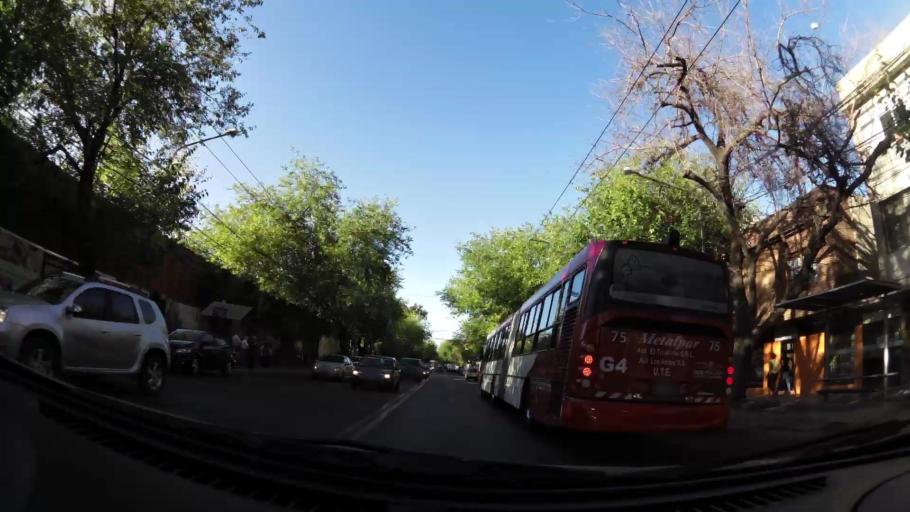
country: AR
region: Mendoza
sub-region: Departamento de Godoy Cruz
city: Godoy Cruz
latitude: -32.9234
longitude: -68.8480
